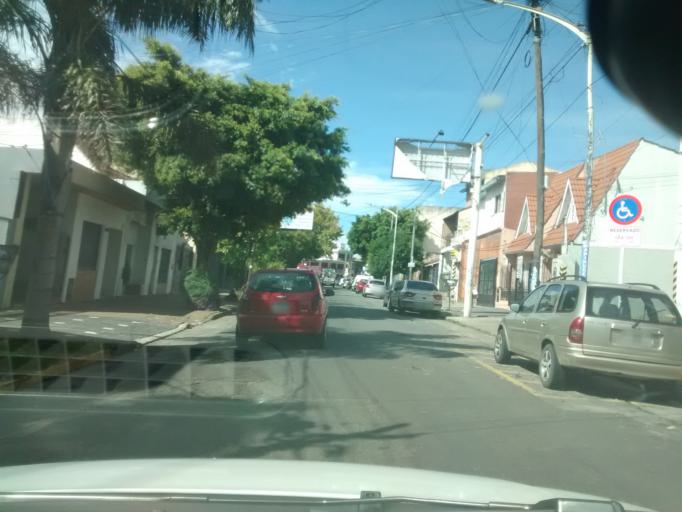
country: AR
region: Buenos Aires
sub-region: Partido de Moron
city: Moron
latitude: -34.6595
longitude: -58.6229
